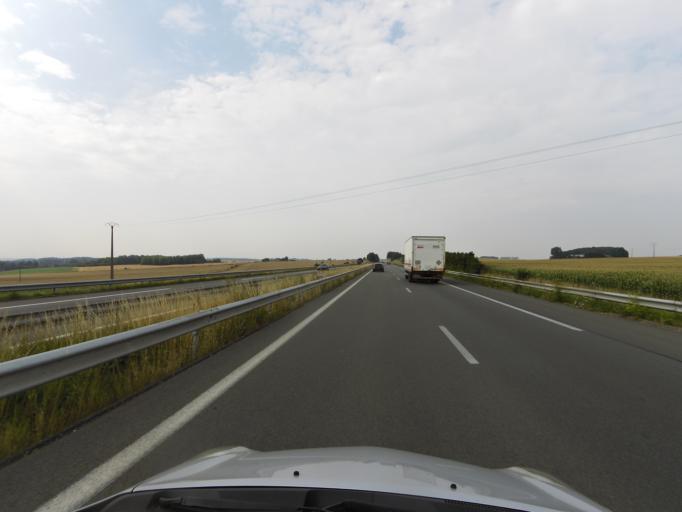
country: FR
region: Picardie
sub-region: Departement de la Somme
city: Epehy
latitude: 49.9557
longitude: 3.2033
